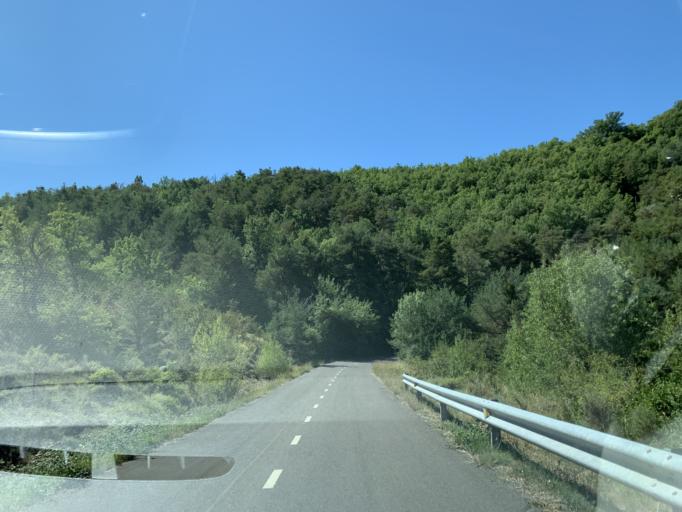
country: ES
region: Aragon
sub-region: Provincia de Huesca
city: Sabinanigo
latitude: 42.5463
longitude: -0.3181
